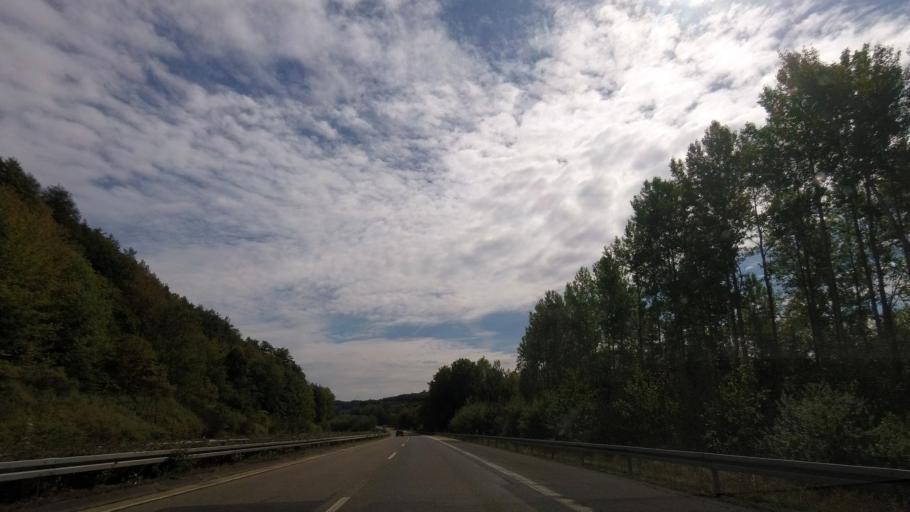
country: DE
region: Hesse
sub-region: Regierungsbezirk Kassel
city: Kirchheim
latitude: 50.8037
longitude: 9.5296
